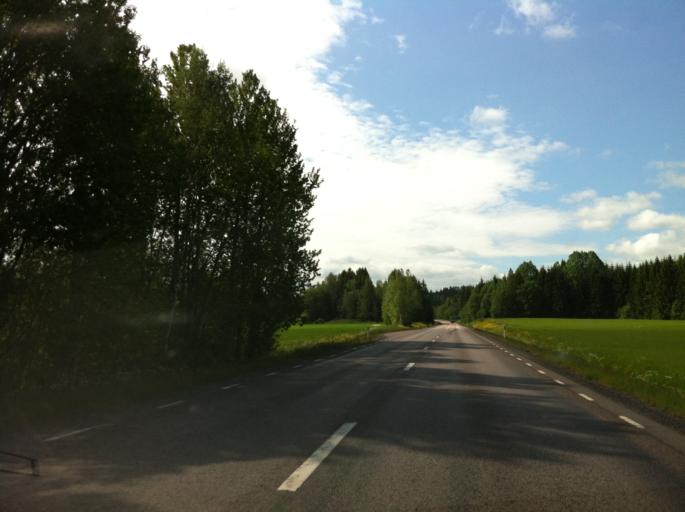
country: SE
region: Vaermland
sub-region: Karlstads Kommun
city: Edsvalla
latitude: 59.4515
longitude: 13.2067
